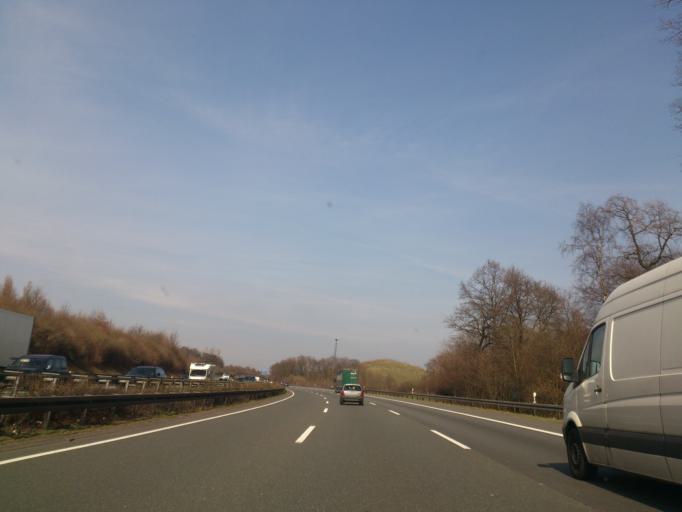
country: DE
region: North Rhine-Westphalia
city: Gevelsberg
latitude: 51.3521
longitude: 7.3642
